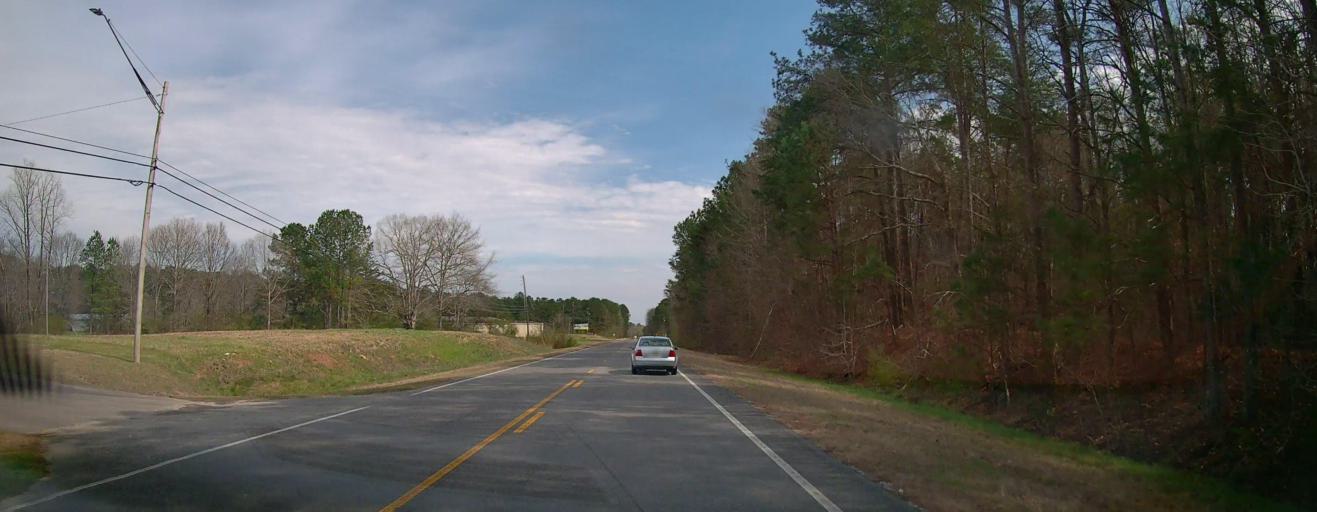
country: US
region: Alabama
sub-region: Walker County
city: Carbon Hill
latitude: 33.9080
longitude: -87.5554
